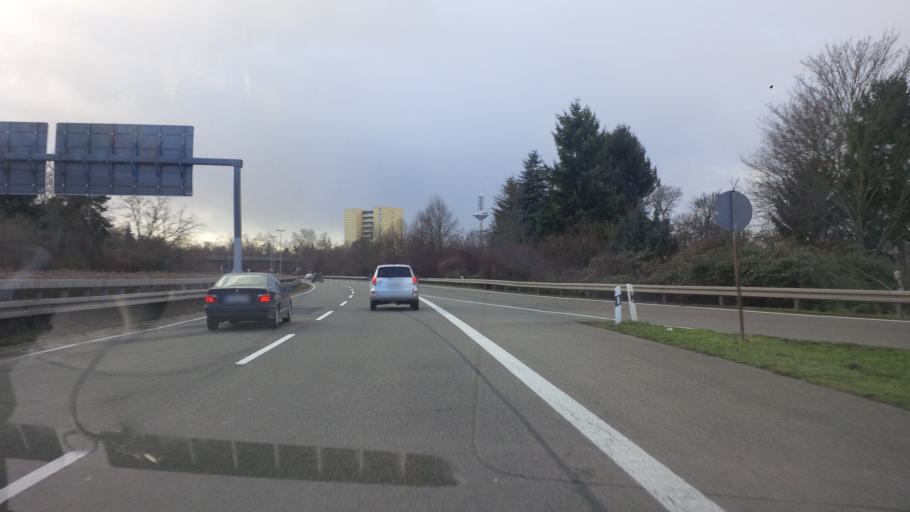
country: DE
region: Hesse
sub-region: Regierungsbezirk Darmstadt
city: Frankfurt am Main
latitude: 50.1561
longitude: 8.6759
